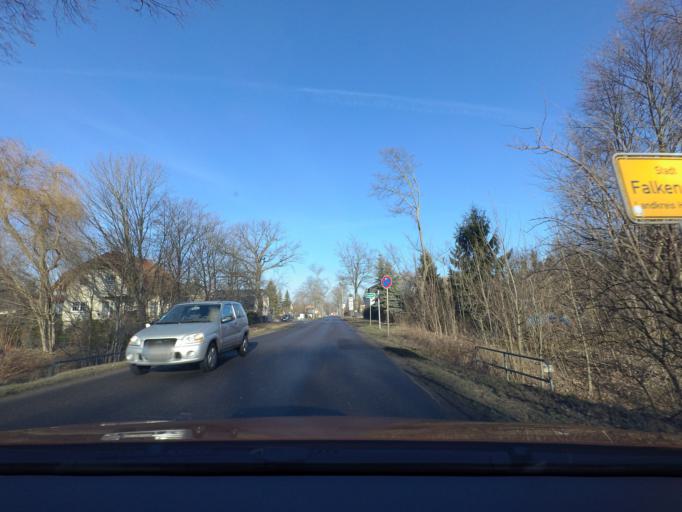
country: DE
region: Brandenburg
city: Falkensee
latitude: 52.5476
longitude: 13.0886
